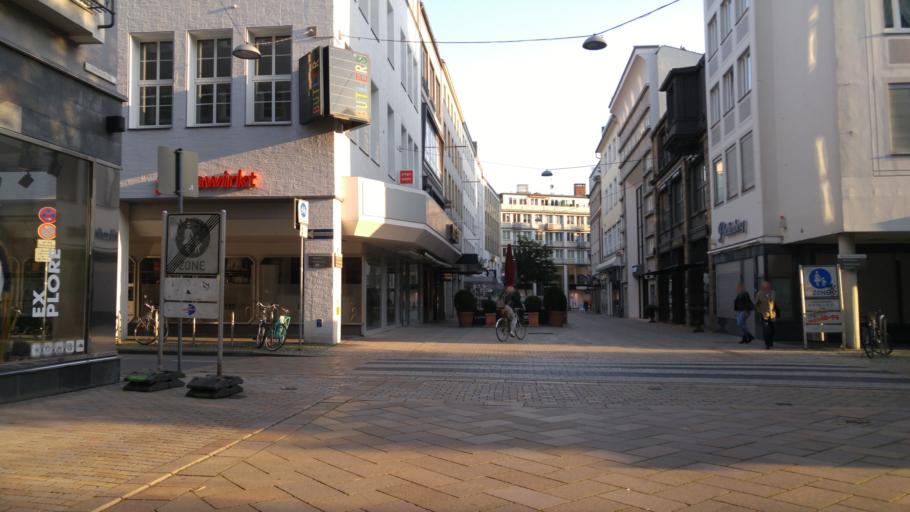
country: DE
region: North Rhine-Westphalia
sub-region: Regierungsbezirk Detmold
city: Bielefeld
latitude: 52.0212
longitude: 8.5318
